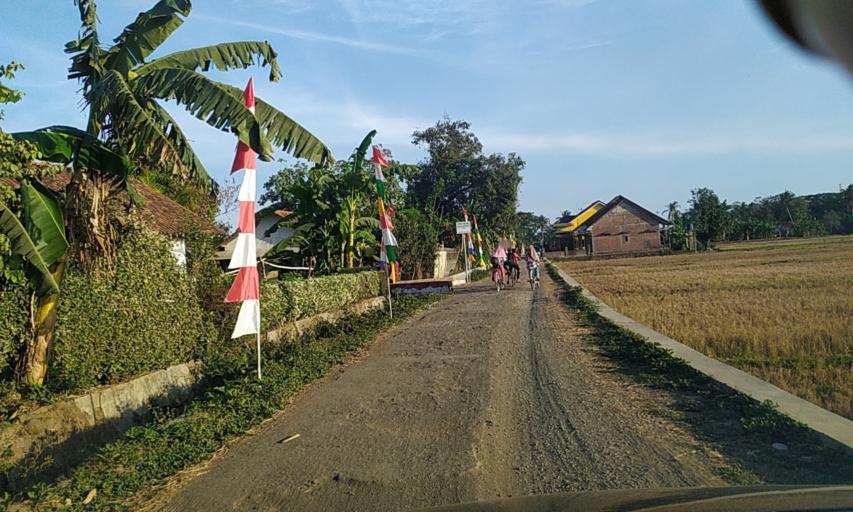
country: ID
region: Central Java
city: Rejanegara
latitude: -7.6926
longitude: 109.0443
